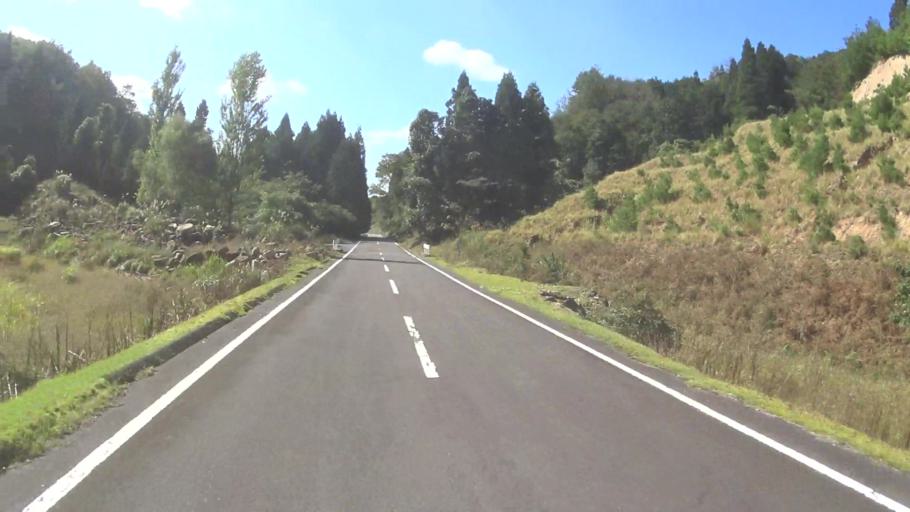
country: JP
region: Hyogo
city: Toyooka
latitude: 35.6093
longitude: 134.9919
